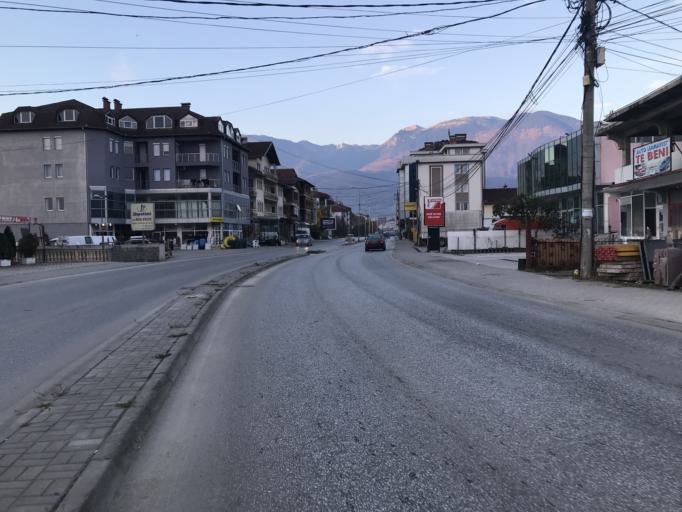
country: XK
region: Pec
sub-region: Komuna e Pejes
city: Peje
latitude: 42.6704
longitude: 20.3088
